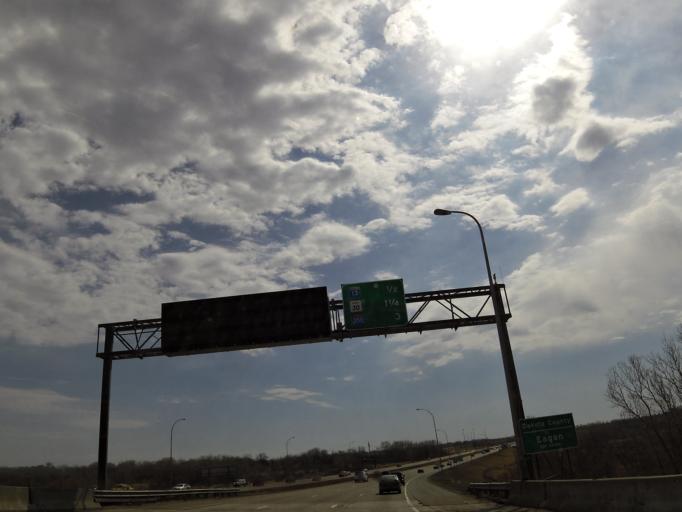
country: US
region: Minnesota
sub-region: Dakota County
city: Eagan
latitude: 44.8246
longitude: -93.2278
